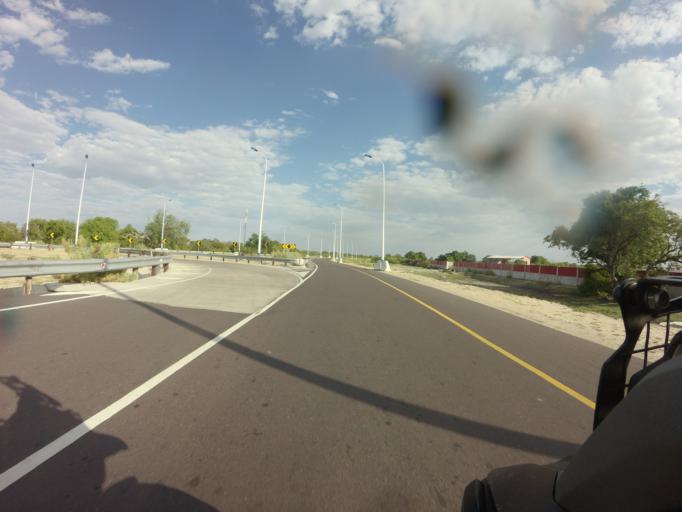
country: AO
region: Cunene
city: Ondjiva
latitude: -17.0102
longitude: 15.6482
